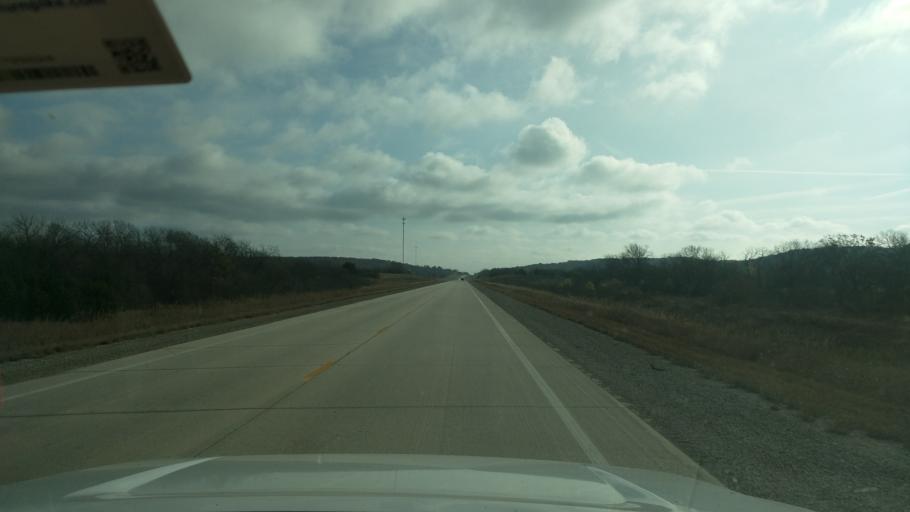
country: US
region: Kansas
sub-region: Chautauqua County
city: Sedan
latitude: 37.0806
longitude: -96.1056
